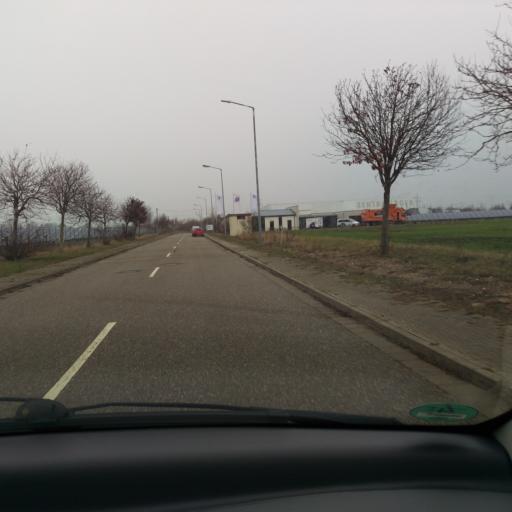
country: DE
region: Saxony-Anhalt
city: Braschwitz
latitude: 51.5142
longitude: 12.0586
